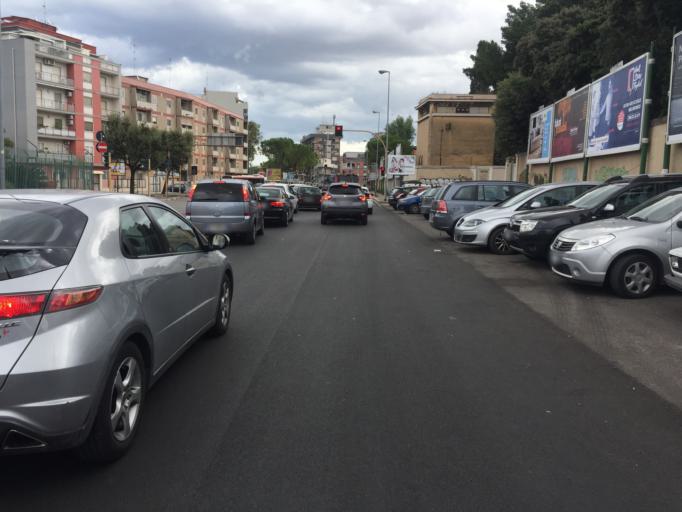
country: IT
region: Apulia
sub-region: Provincia di Bari
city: Bari
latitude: 41.1074
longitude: 16.8580
